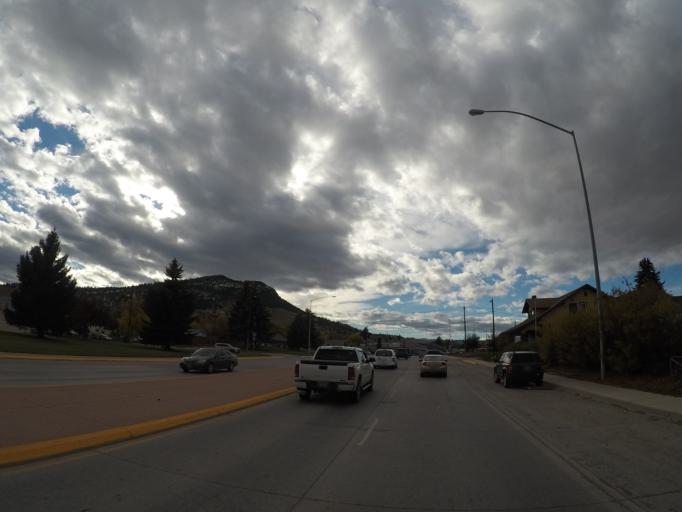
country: US
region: Montana
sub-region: Lewis and Clark County
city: Helena
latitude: 46.5981
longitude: -112.0390
